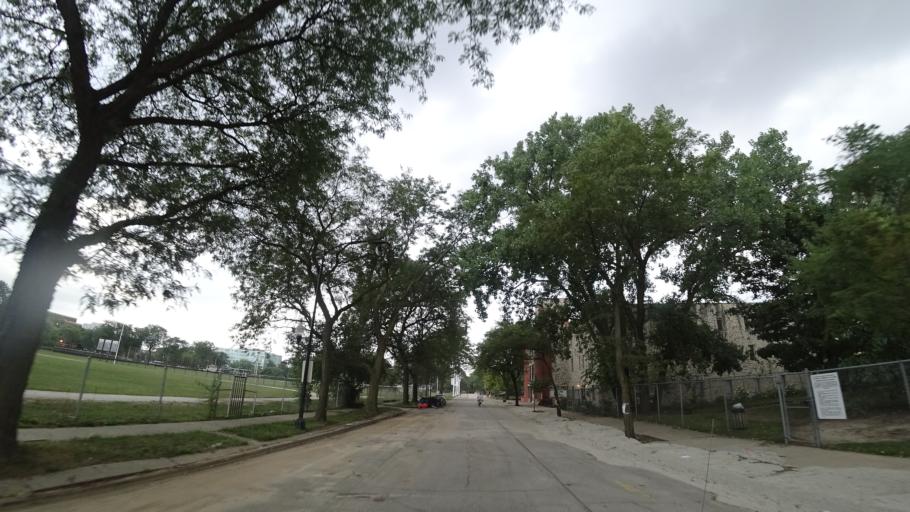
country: US
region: Illinois
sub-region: Cook County
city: Chicago
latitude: 41.8404
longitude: -87.6252
